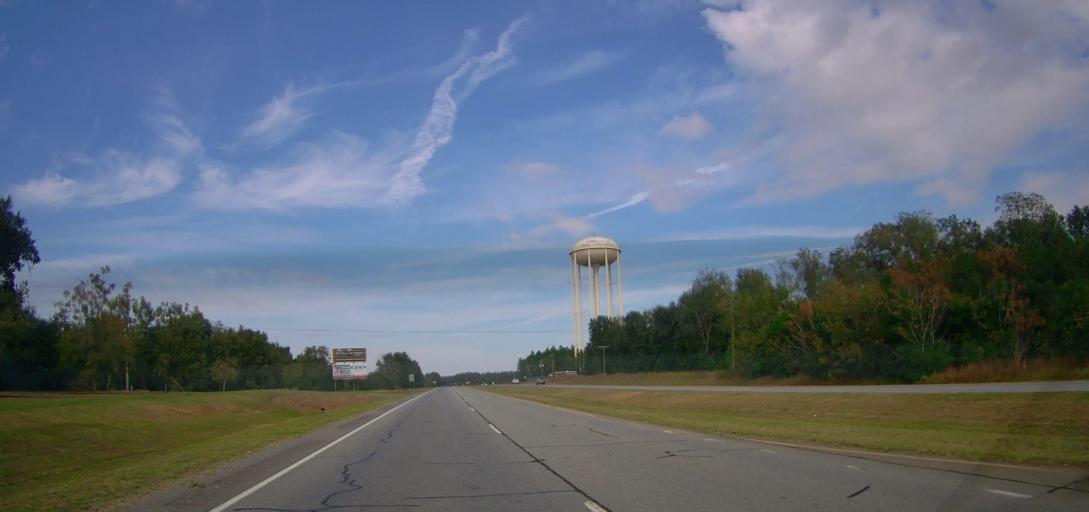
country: US
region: Georgia
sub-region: Mitchell County
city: Camilla
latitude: 31.2721
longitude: -84.1920
